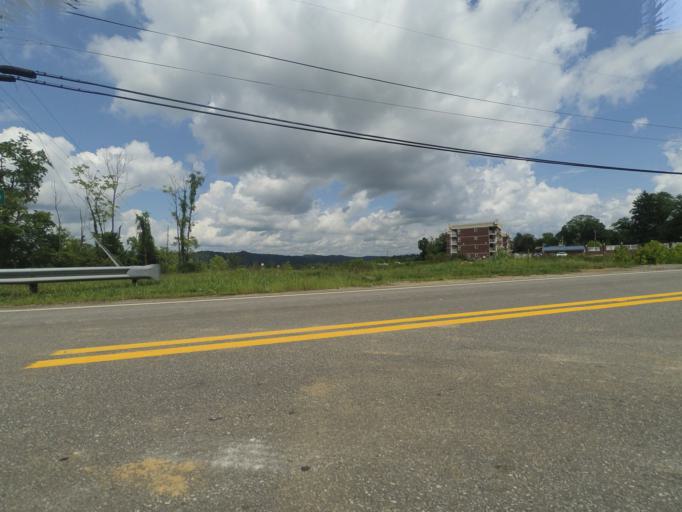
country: US
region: West Virginia
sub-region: Cabell County
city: Pea Ridge
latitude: 38.4104
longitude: -82.3493
